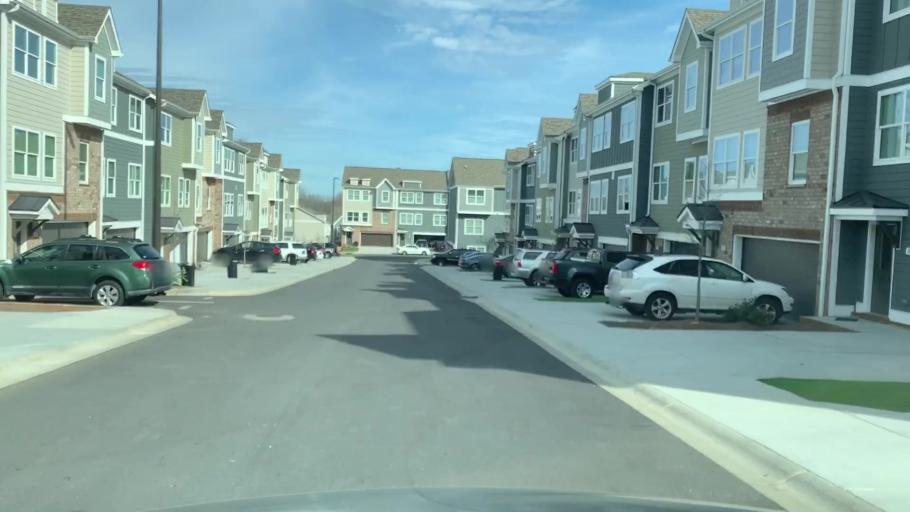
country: US
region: South Carolina
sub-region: Pickens County
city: Central
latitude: 34.6918
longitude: -82.7857
